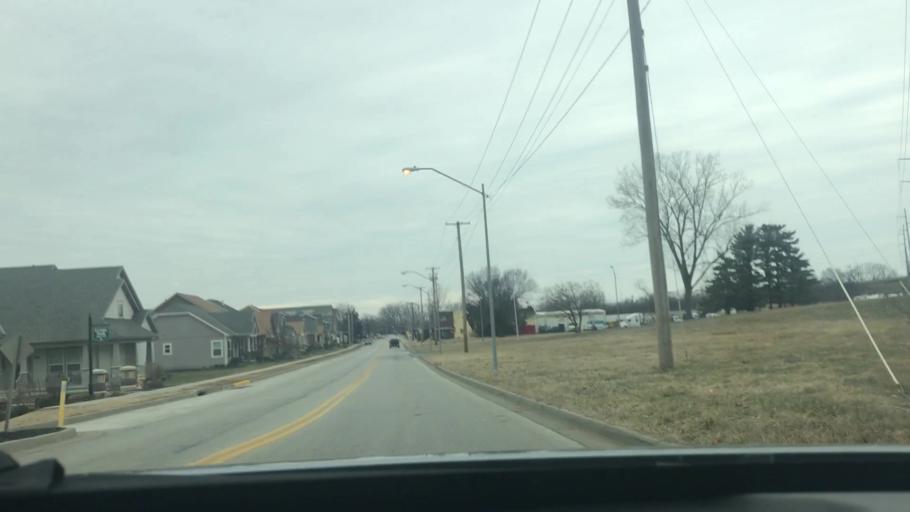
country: US
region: Missouri
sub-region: Clay County
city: North Kansas City
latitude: 39.1523
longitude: -94.5728
